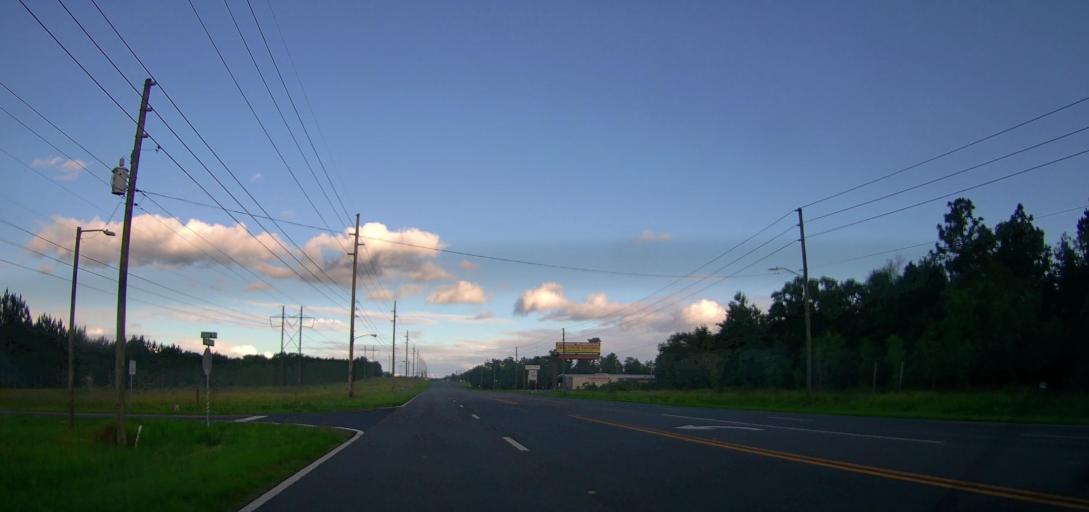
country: US
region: Florida
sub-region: Marion County
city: Silver Springs Shores
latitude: 29.0944
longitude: -82.0022
